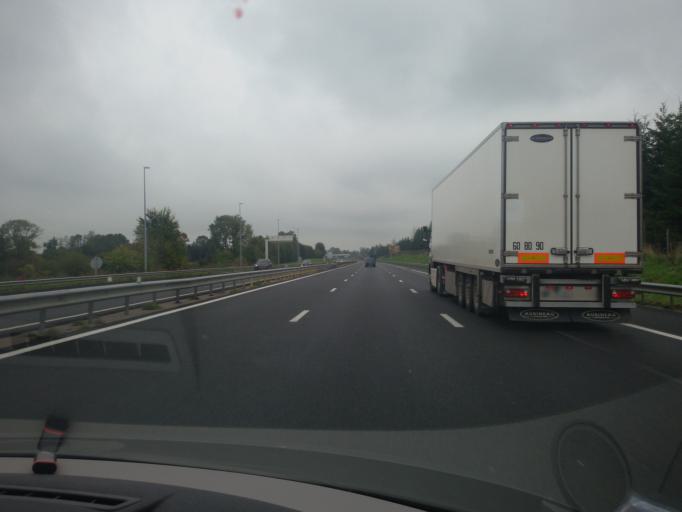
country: FR
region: Haute-Normandie
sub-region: Departement de l'Eure
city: Beuzeville
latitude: 49.3254
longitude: 0.3317
